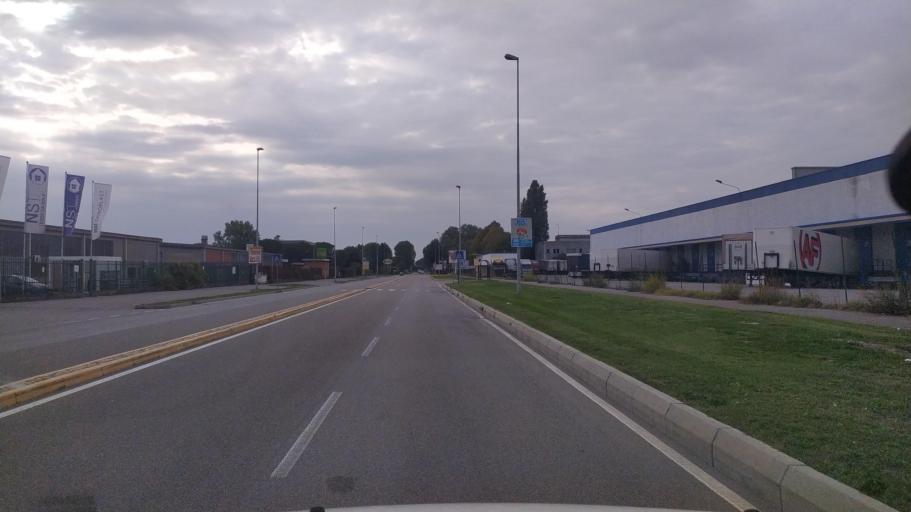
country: IT
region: Lombardy
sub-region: Citta metropolitana di Milano
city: Cusago
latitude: 45.4382
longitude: 9.0454
